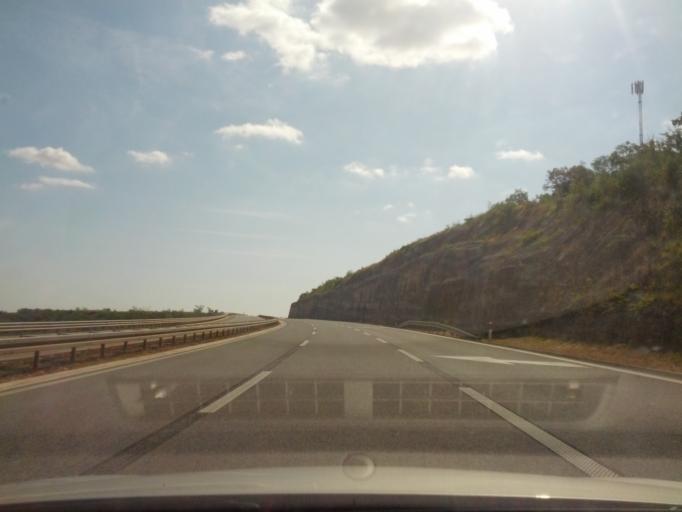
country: HR
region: Istarska
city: Buje
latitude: 45.3232
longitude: 13.6511
